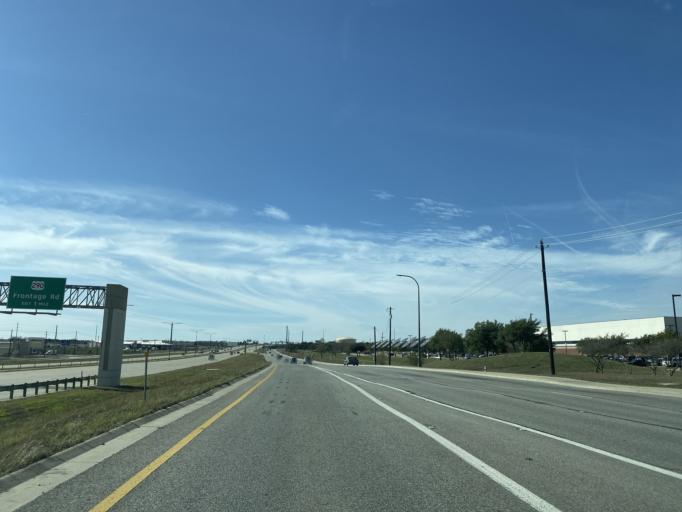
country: US
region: Texas
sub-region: Travis County
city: Manor
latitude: 30.3339
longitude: -97.6116
